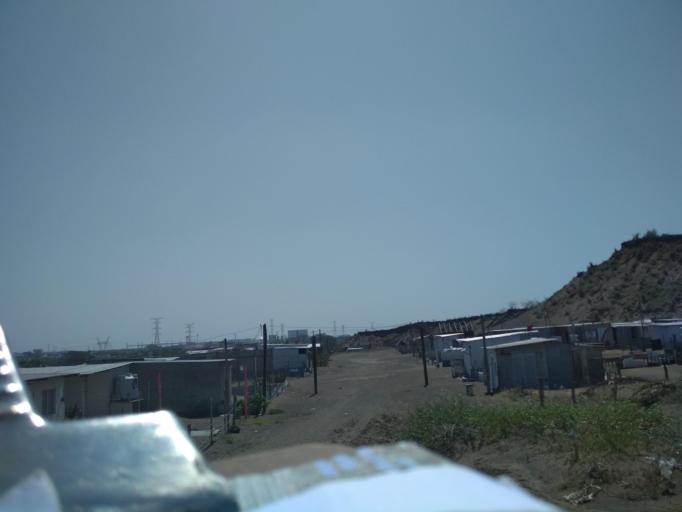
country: MX
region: Veracruz
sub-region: Veracruz
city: Lomas de Rio Medio Cuatro
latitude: 19.1901
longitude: -96.1974
